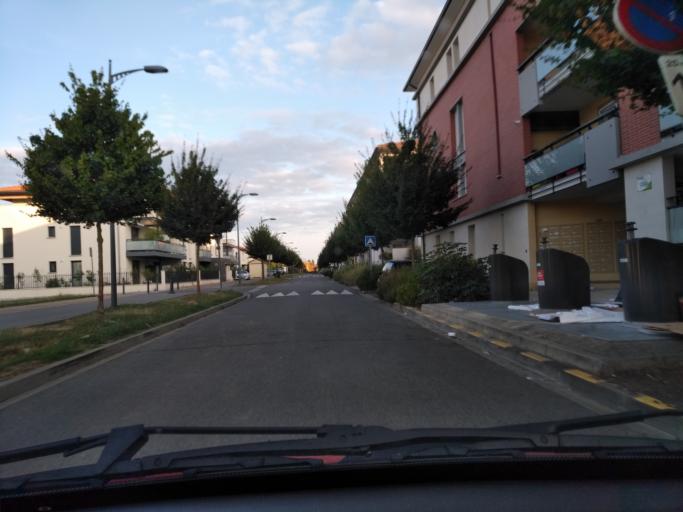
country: FR
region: Midi-Pyrenees
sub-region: Departement de la Haute-Garonne
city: Colomiers
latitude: 43.6218
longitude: 1.3296
